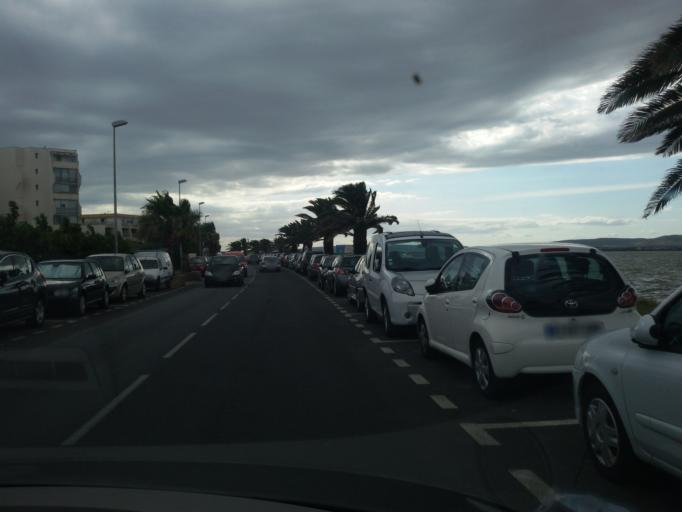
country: FR
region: Languedoc-Roussillon
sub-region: Departement de l'Herault
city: Palavas-les-Flots
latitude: 43.5230
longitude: 3.9189
